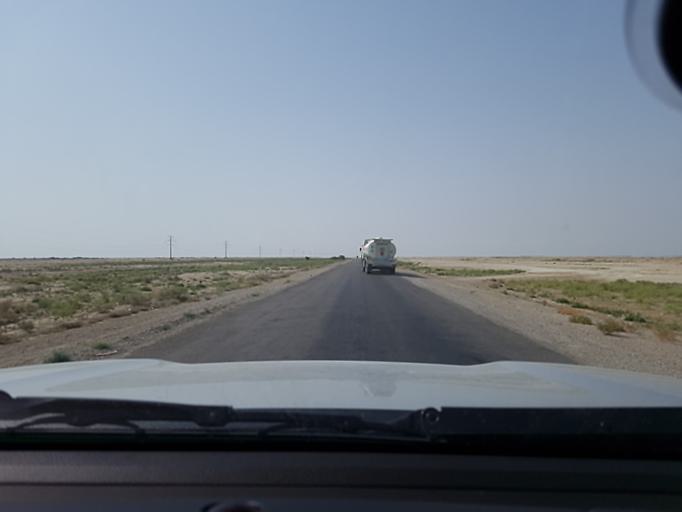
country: TM
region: Balkan
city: Gumdag
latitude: 38.8601
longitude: 54.5949
